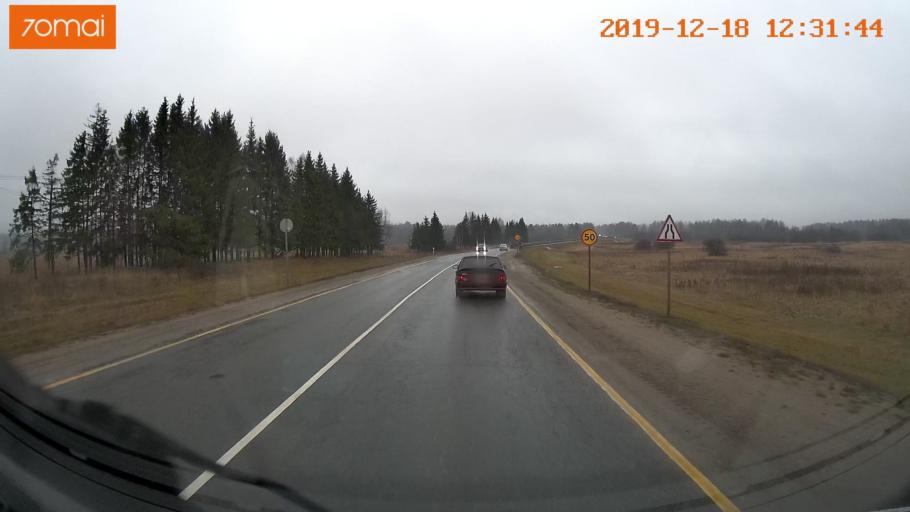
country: RU
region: Moskovskaya
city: Rumyantsevo
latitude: 56.1017
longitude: 36.5442
